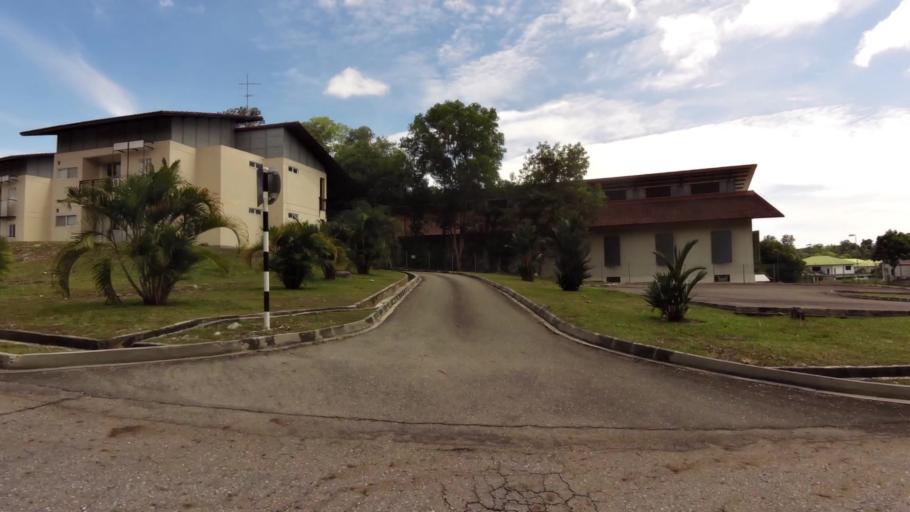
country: BN
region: Brunei and Muara
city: Bandar Seri Begawan
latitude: 4.9349
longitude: 114.8922
